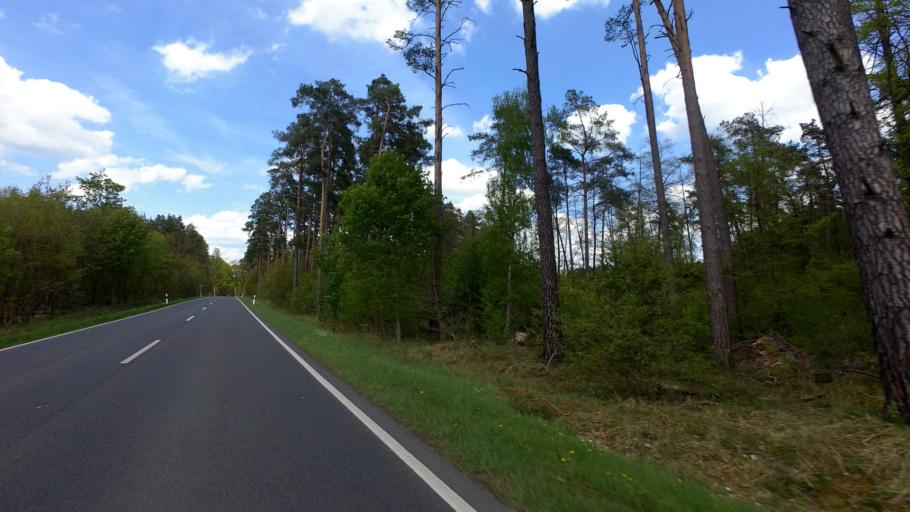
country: DE
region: Brandenburg
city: Friedrichswalde
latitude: 52.9815
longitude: 13.5834
